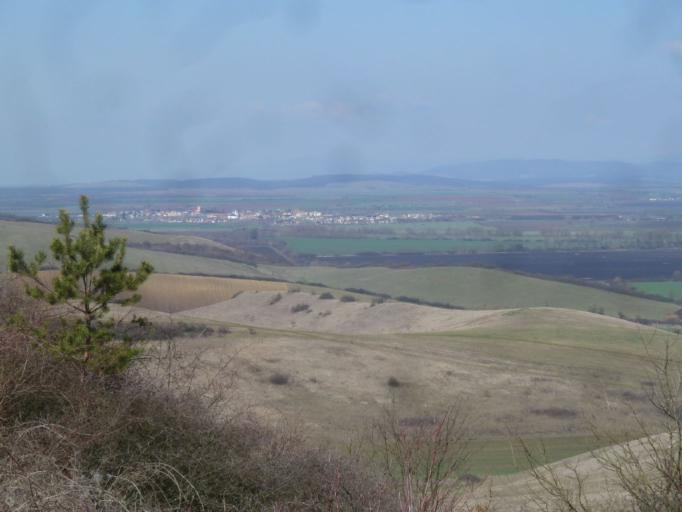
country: HU
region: Borsod-Abauj-Zemplen
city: Ozd
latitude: 48.2726
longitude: 20.3064
